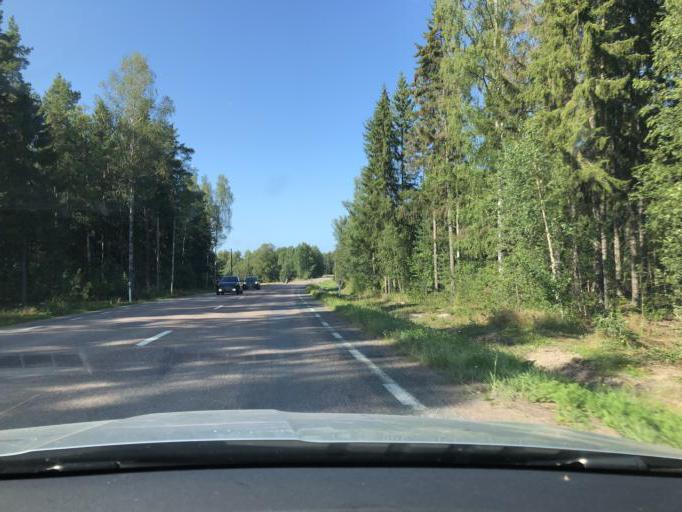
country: SE
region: Dalarna
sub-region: Faluns Kommun
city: Falun
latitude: 60.5063
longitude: 15.7391
